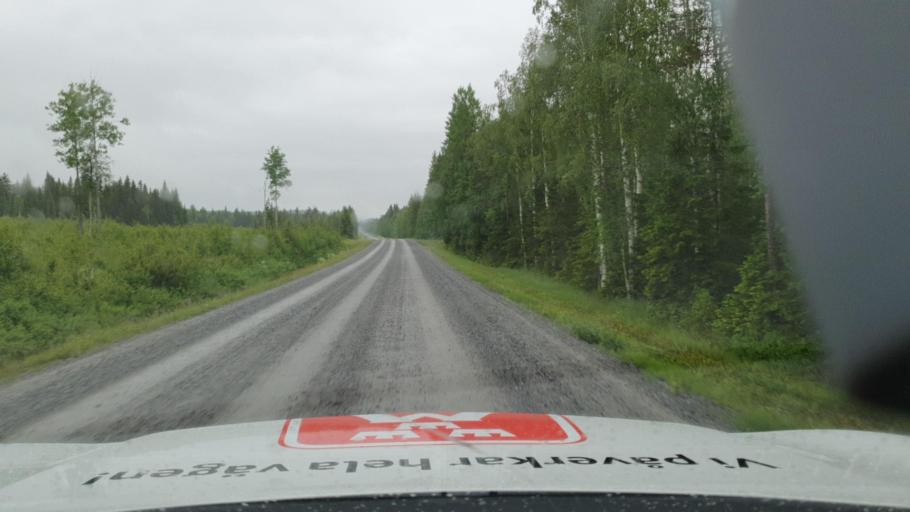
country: SE
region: Vaesterbotten
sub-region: Nordmalings Kommun
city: Nordmaling
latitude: 63.8356
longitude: 19.4853
